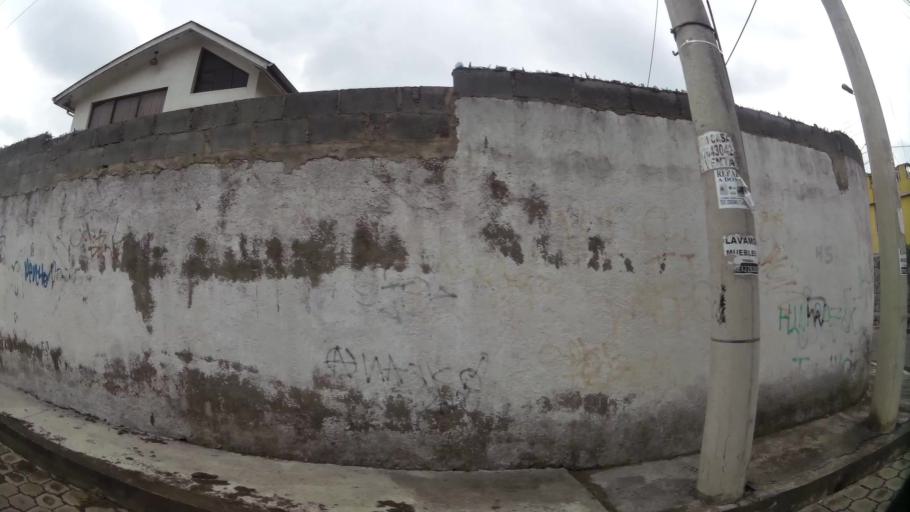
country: EC
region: Pichincha
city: Sangolqui
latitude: -0.2967
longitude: -78.4671
